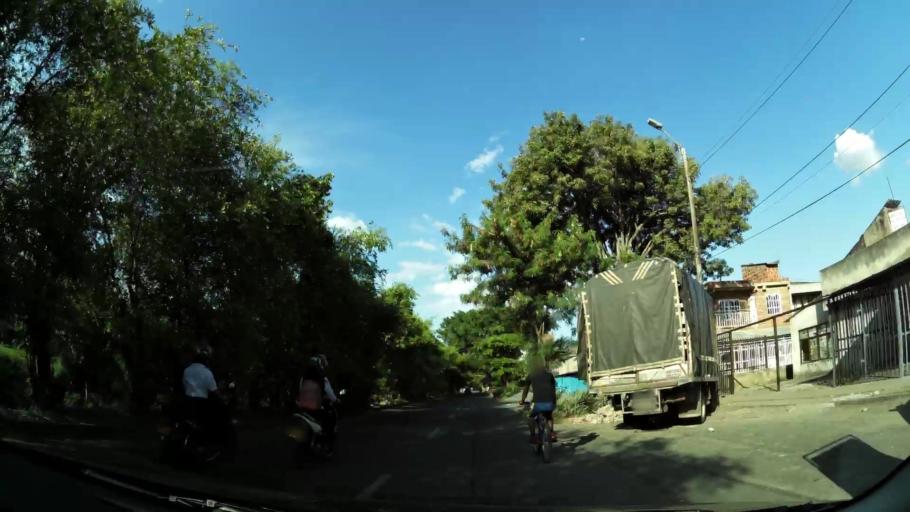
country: CO
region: Valle del Cauca
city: Cali
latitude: 3.4039
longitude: -76.5087
